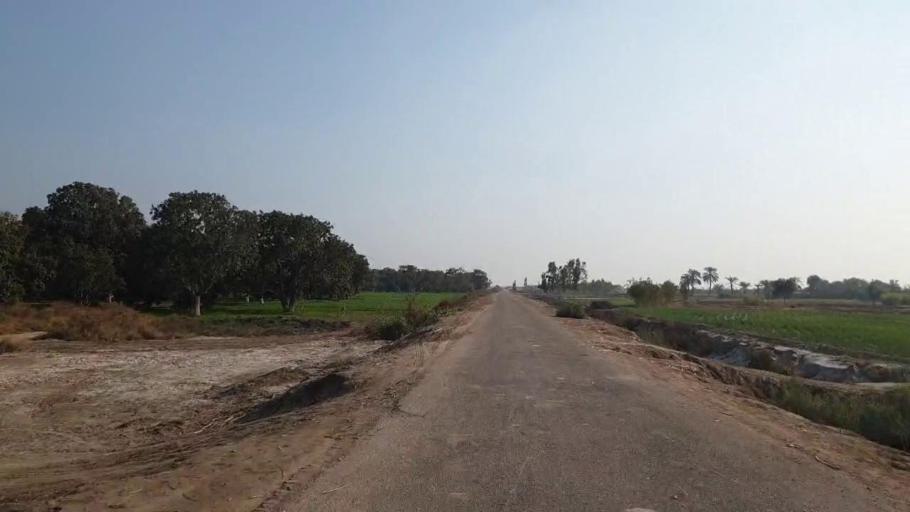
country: PK
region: Sindh
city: Tando Allahyar
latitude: 25.5969
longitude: 68.6179
